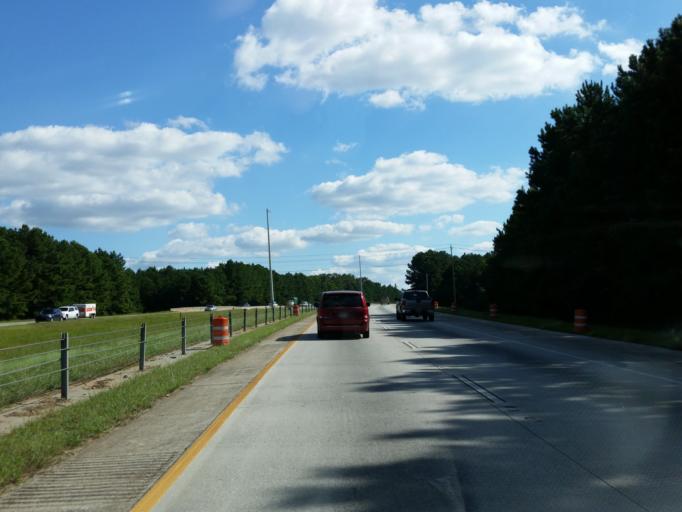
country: US
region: Georgia
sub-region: Henry County
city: Stockbridge
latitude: 33.5551
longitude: -84.2692
